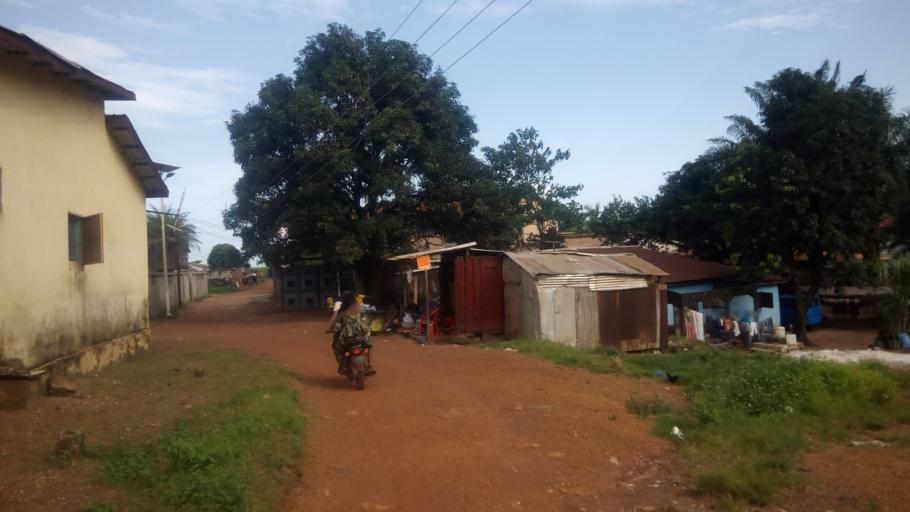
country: GN
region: Kindia
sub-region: Prefecture de Dubreka
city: Dubreka
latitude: 9.6491
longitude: -13.5338
